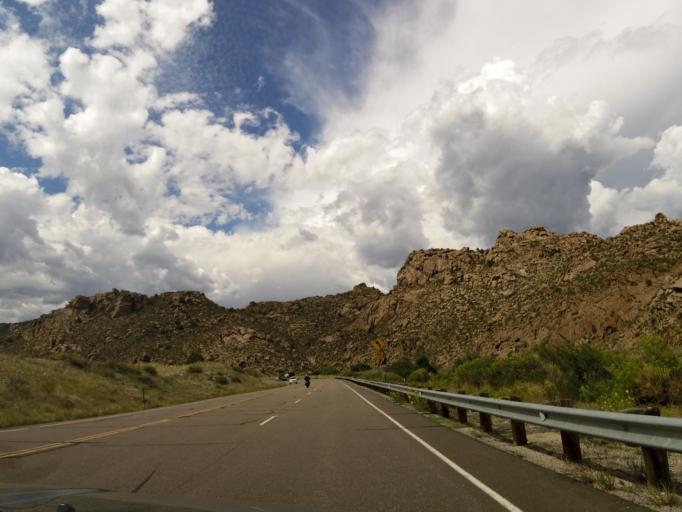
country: US
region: Colorado
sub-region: Custer County
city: Westcliffe
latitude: 38.3950
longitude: -105.6288
